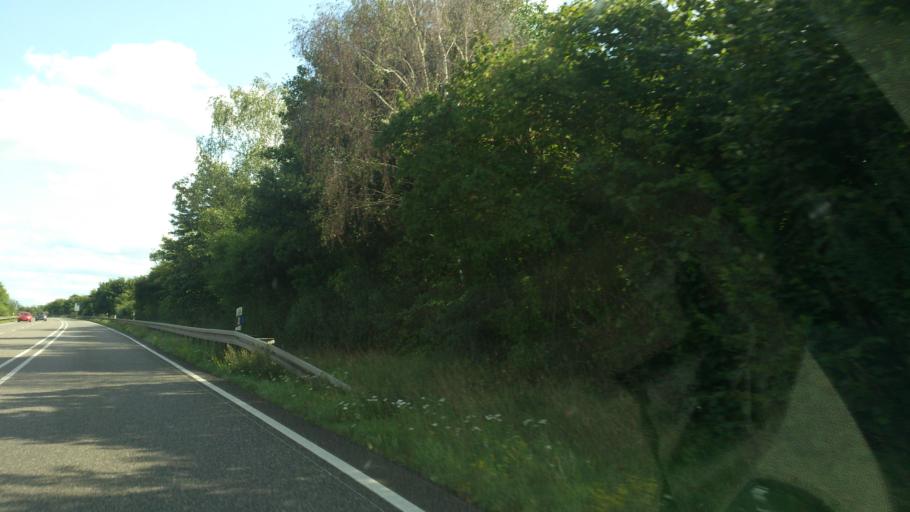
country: DE
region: North Rhine-Westphalia
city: Zulpich
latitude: 50.6864
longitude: 6.7053
